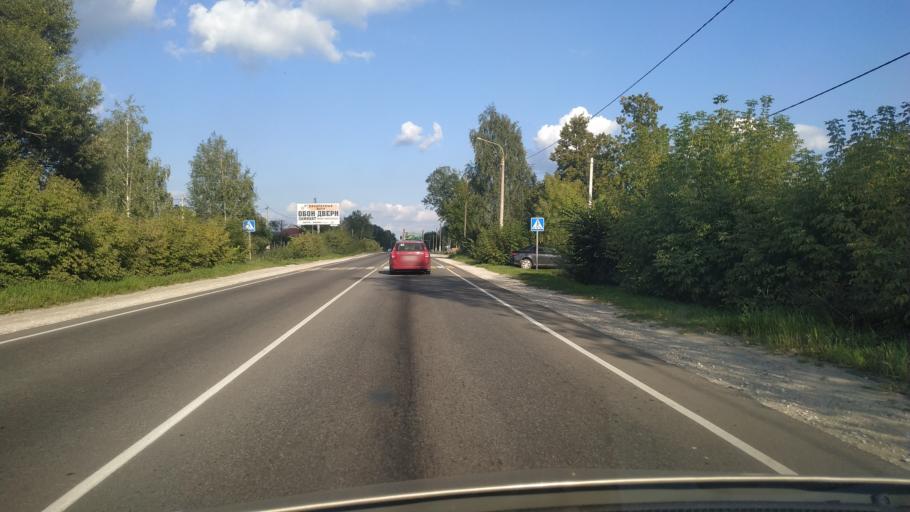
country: RU
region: Moskovskaya
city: Shaturtorf
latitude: 55.5795
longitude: 39.4728
